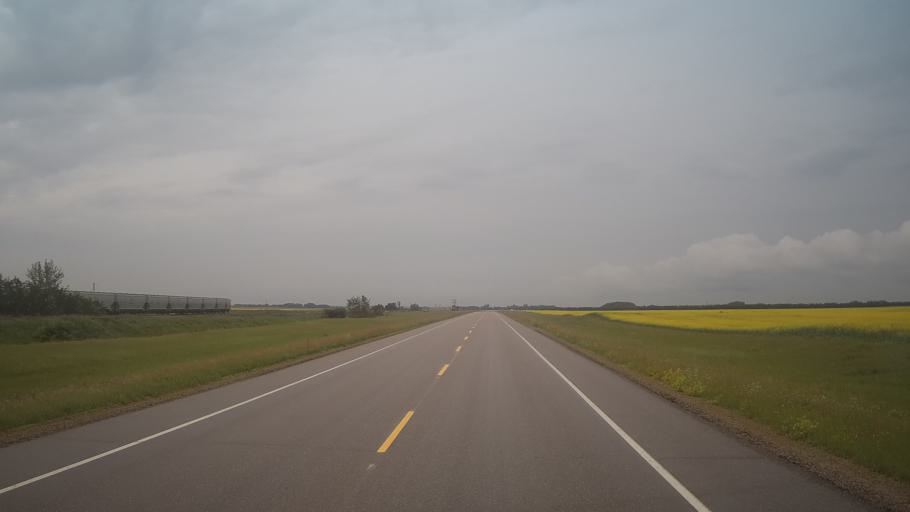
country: CA
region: Saskatchewan
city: Wilkie
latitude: 52.3059
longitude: -108.6829
